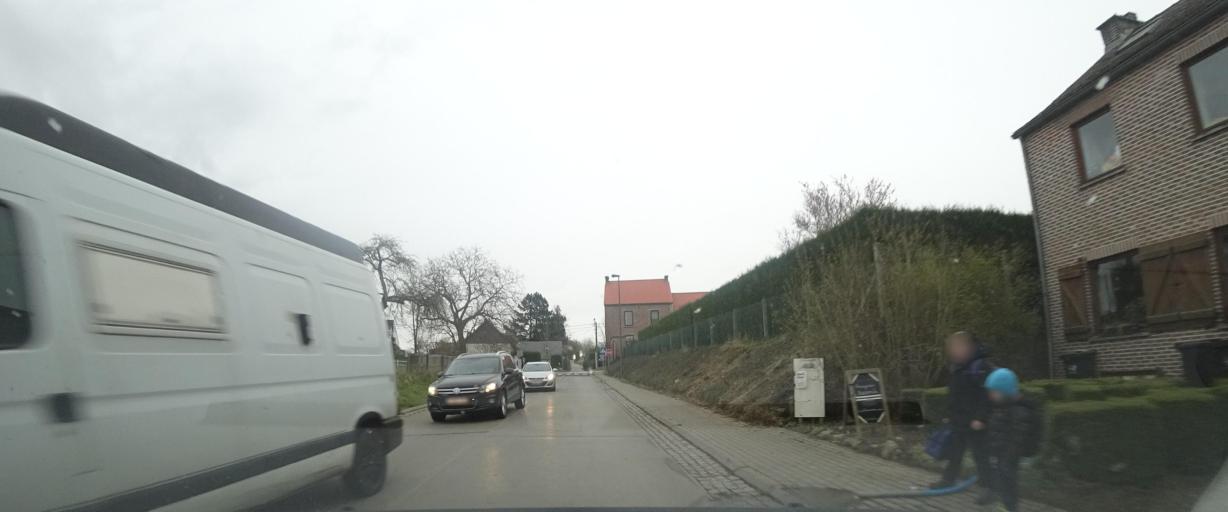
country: BE
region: Wallonia
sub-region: Province du Brabant Wallon
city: Chastre-Villeroux-Blanmont
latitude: 50.6192
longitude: 4.6447
